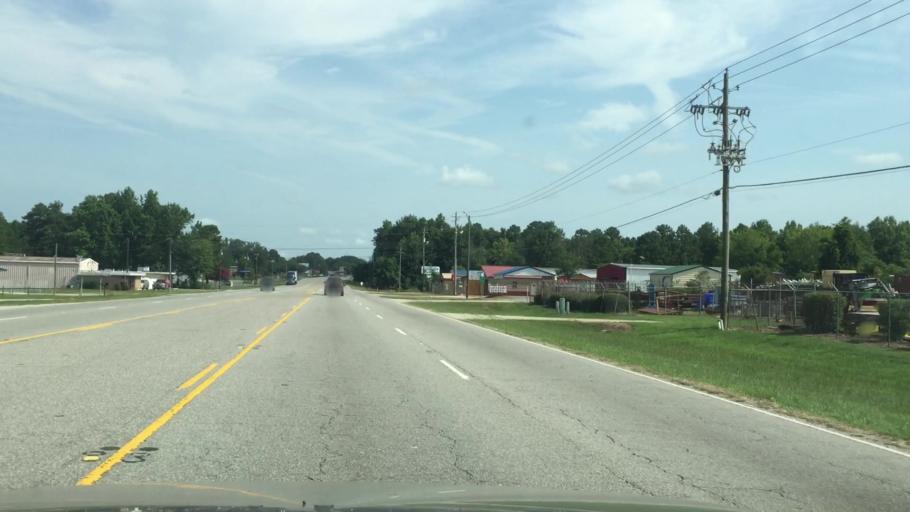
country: US
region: South Carolina
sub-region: Sumter County
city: South Sumter
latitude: 33.8950
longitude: -80.3523
